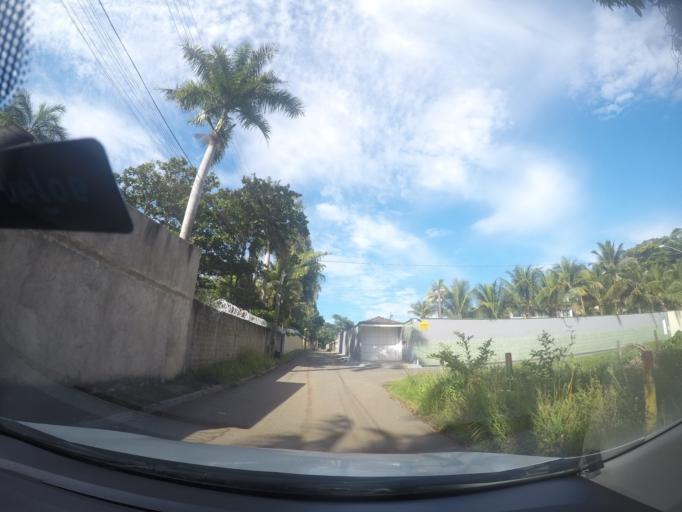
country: BR
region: Goias
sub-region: Goiania
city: Goiania
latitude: -16.6653
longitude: -49.2030
